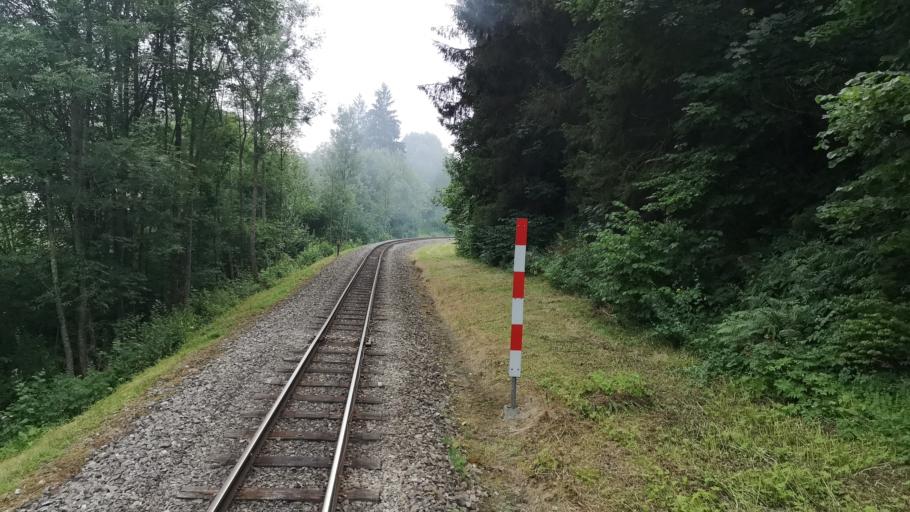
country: AT
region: Styria
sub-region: Politischer Bezirk Murau
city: Murau
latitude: 47.1124
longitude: 14.1605
